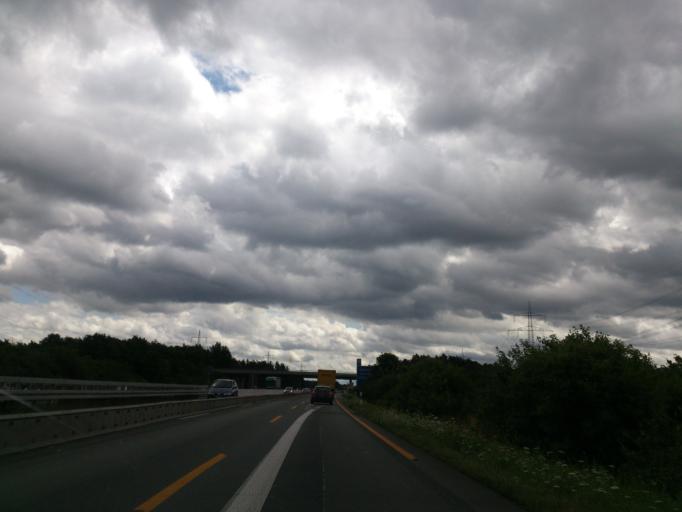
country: DE
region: North Rhine-Westphalia
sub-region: Regierungsbezirk Detmold
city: Hovelhof
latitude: 51.8590
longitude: 8.6652
